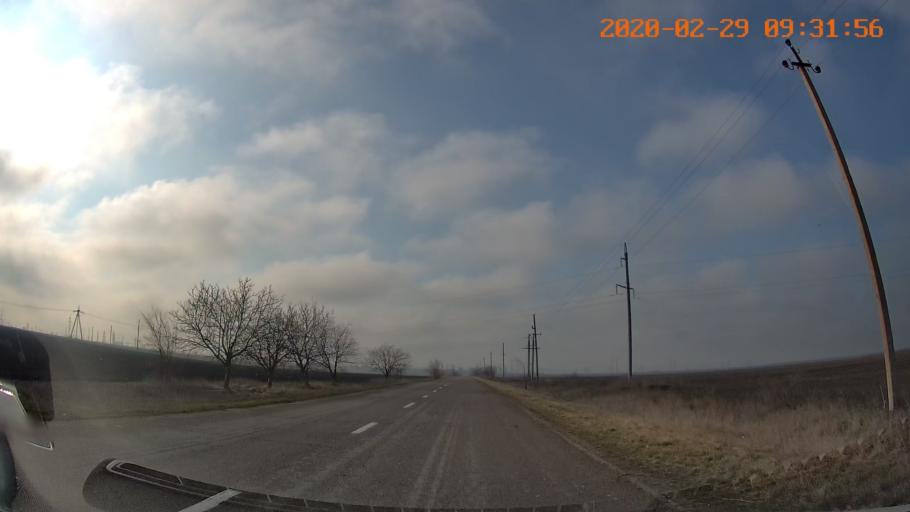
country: MD
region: Telenesti
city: Dnestrovsc
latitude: 46.6462
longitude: 29.9086
